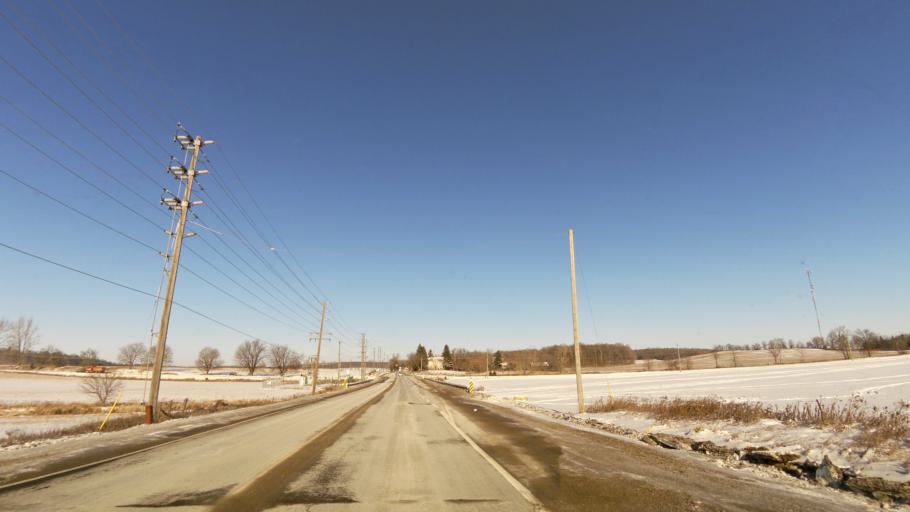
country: CA
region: Ontario
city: Quinte West
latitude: 44.2113
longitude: -77.8251
